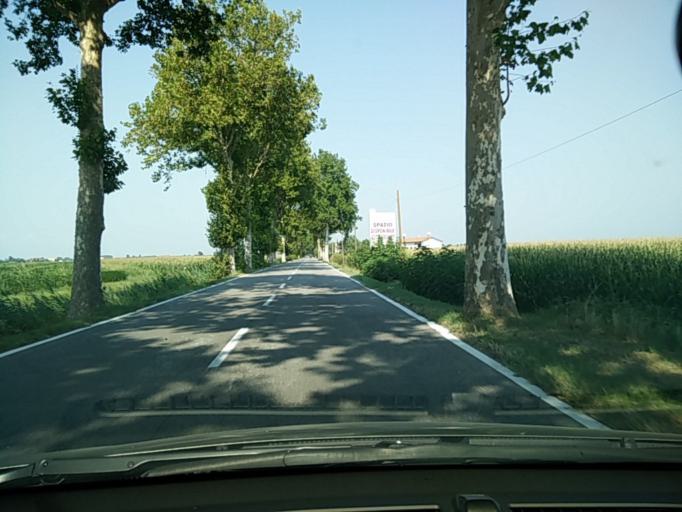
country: IT
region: Veneto
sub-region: Provincia di Venezia
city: San Giorgio di Livenza
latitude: 45.6421
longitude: 12.7583
